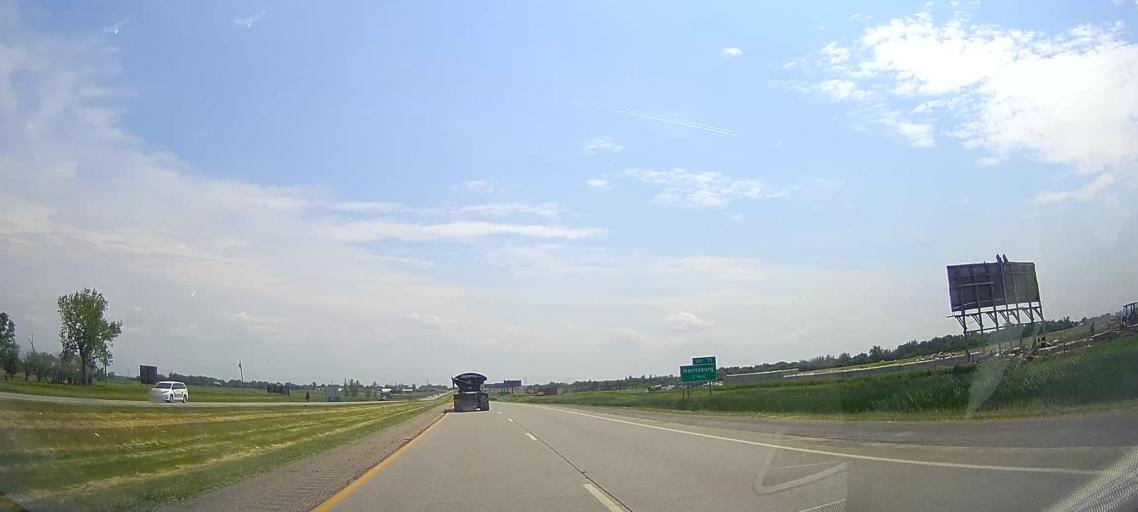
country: US
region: South Dakota
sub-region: Lincoln County
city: Tea
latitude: 43.4512
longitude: -96.7983
